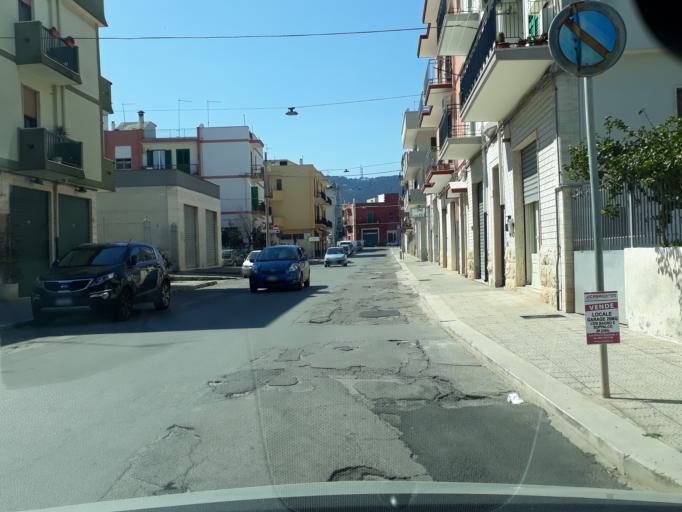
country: IT
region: Apulia
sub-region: Provincia di Brindisi
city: Fasano
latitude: 40.8394
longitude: 17.3616
